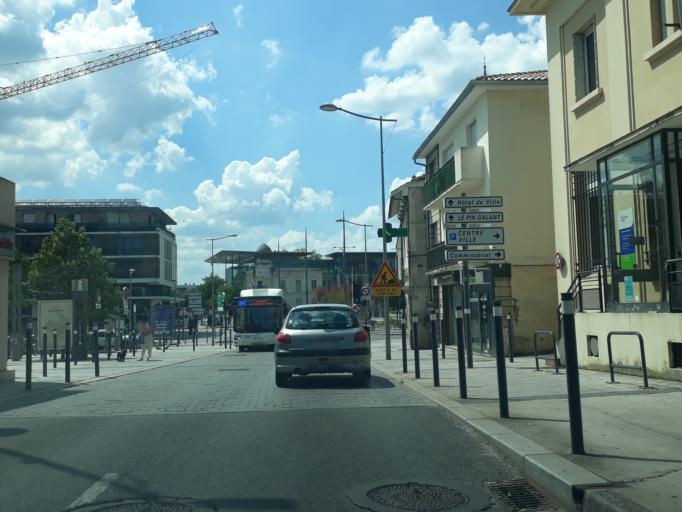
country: FR
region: Aquitaine
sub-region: Departement de la Gironde
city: Merignac
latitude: 44.8416
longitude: -0.6459
